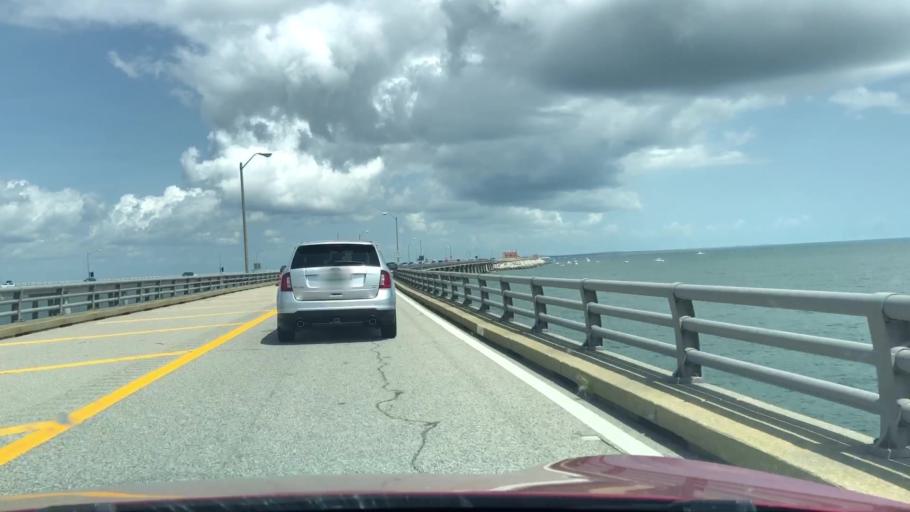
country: US
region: Virginia
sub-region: City of Virginia Beach
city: Virginia Beach
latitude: 37.0294
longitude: -76.0857
